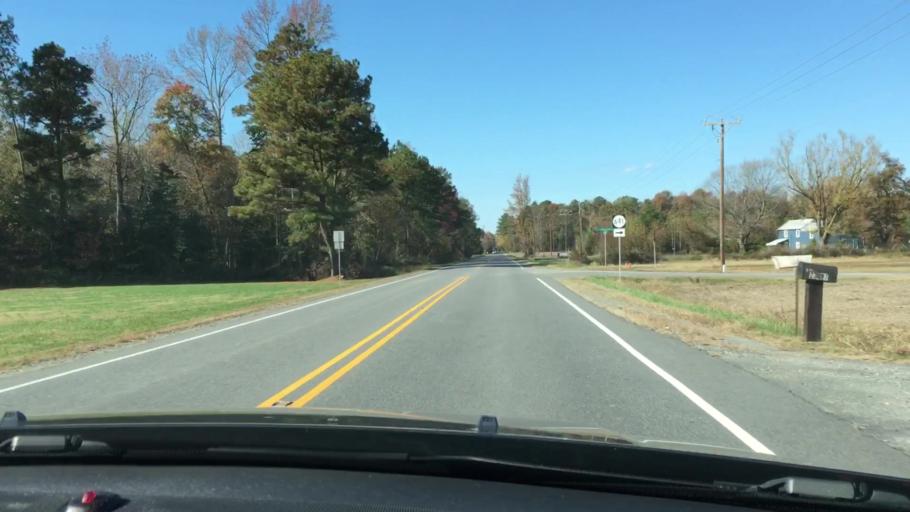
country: US
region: Virginia
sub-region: King William County
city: King William
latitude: 37.6610
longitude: -76.9598
